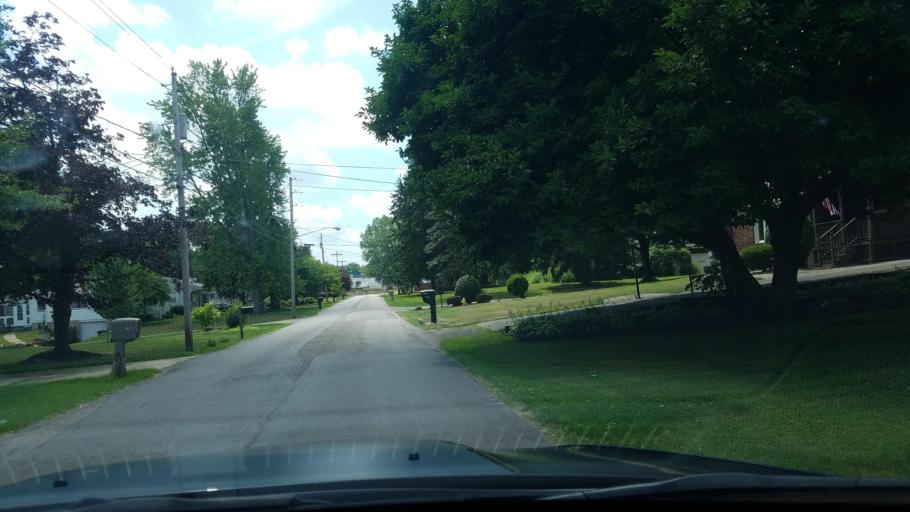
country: US
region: Ohio
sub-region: Trumbull County
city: Bolindale
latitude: 41.2211
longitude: -80.7767
